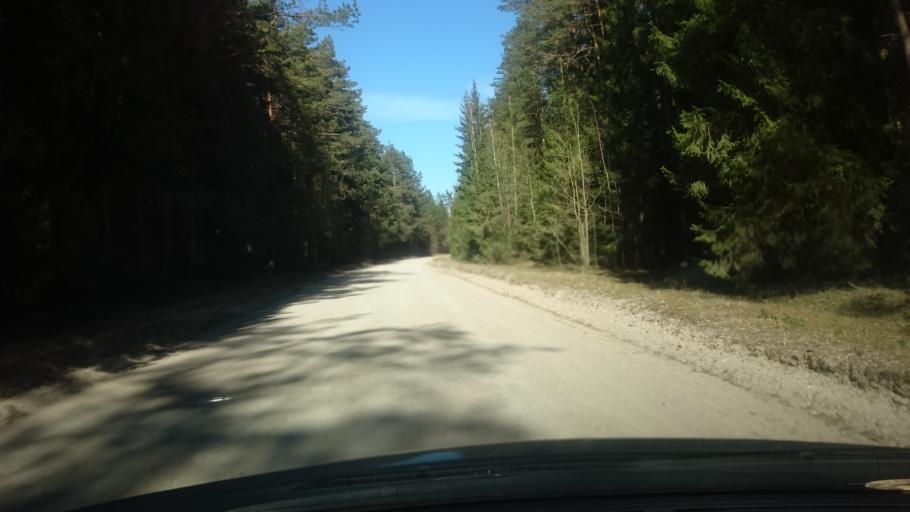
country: EE
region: Polvamaa
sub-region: Polva linn
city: Polva
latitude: 58.1533
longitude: 27.0524
